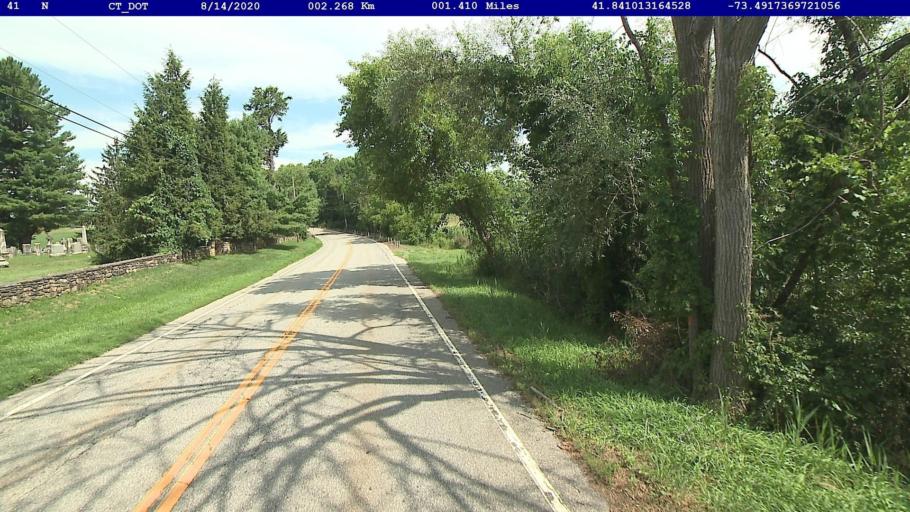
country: US
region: Connecticut
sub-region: Litchfield County
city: Kent
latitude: 41.8410
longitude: -73.4917
